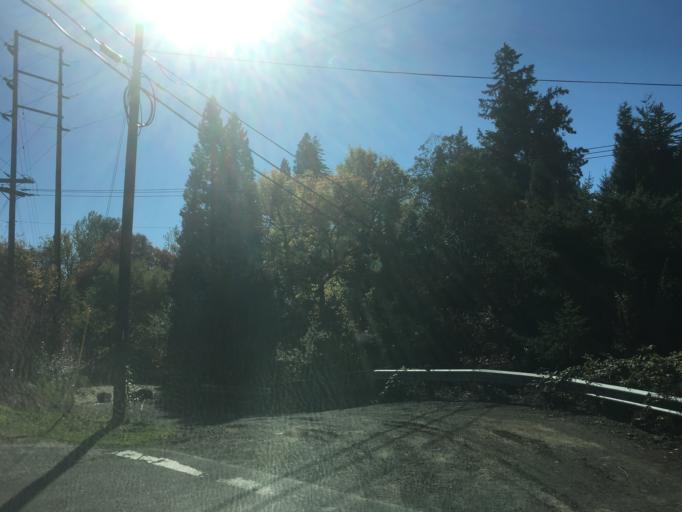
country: US
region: Oregon
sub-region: Multnomah County
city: Gresham
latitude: 45.4808
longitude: -122.4138
